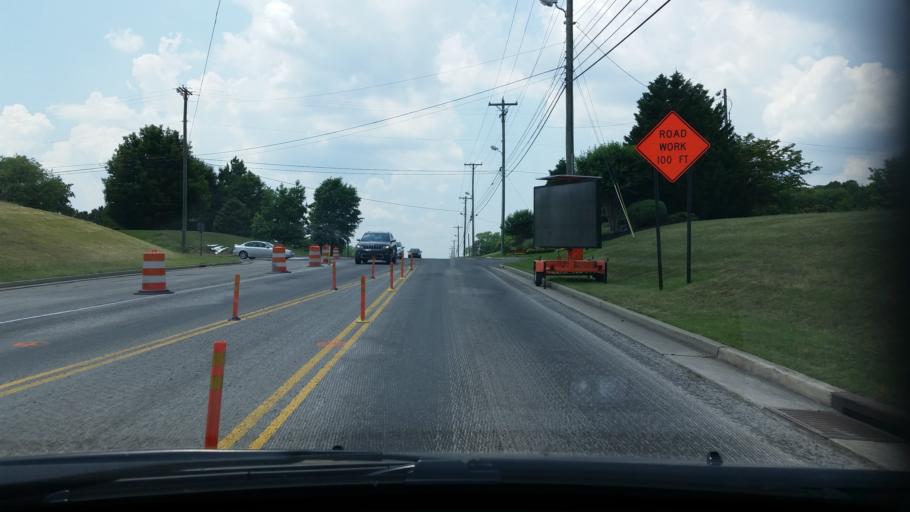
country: US
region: Tennessee
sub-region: Williamson County
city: Brentwood Estates
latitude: 35.9938
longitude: -86.7600
